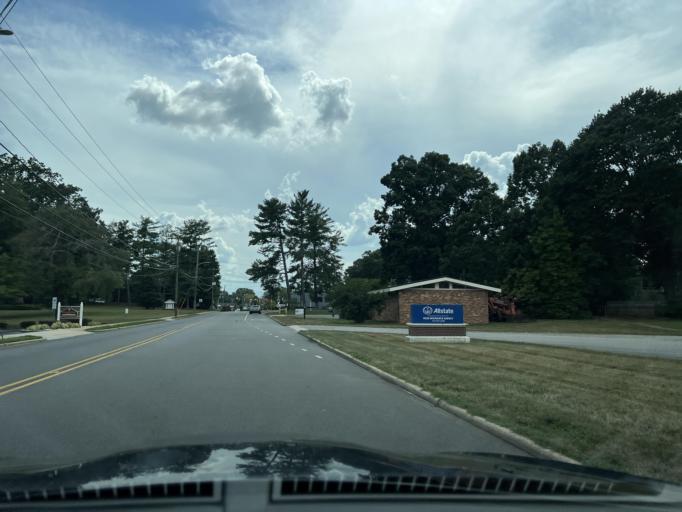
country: US
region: North Carolina
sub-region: Iredell County
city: Statesville
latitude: 35.7964
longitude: -80.8715
